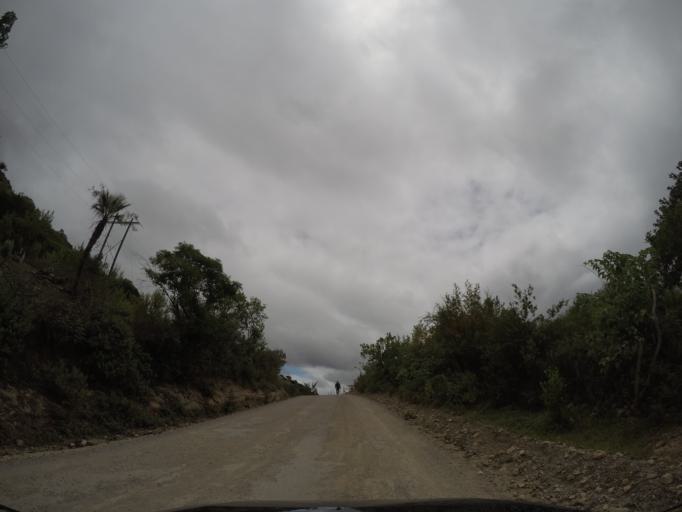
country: MX
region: Oaxaca
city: San Lorenzo Albarradas
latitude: 16.8895
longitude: -96.2647
